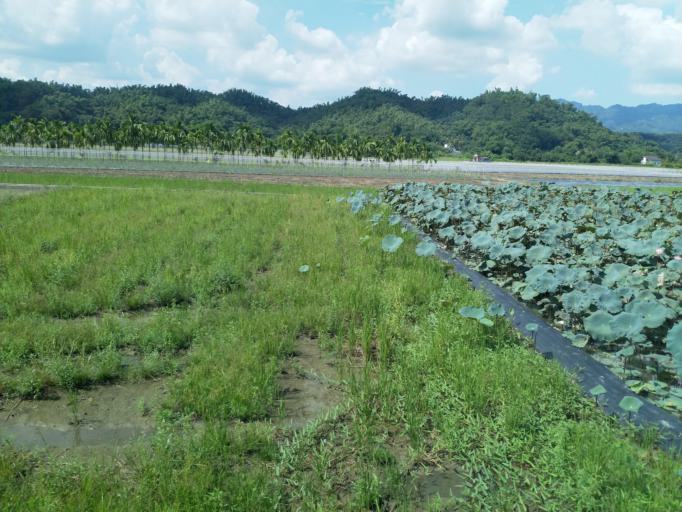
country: TW
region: Taiwan
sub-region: Pingtung
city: Pingtung
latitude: 22.8845
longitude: 120.5776
